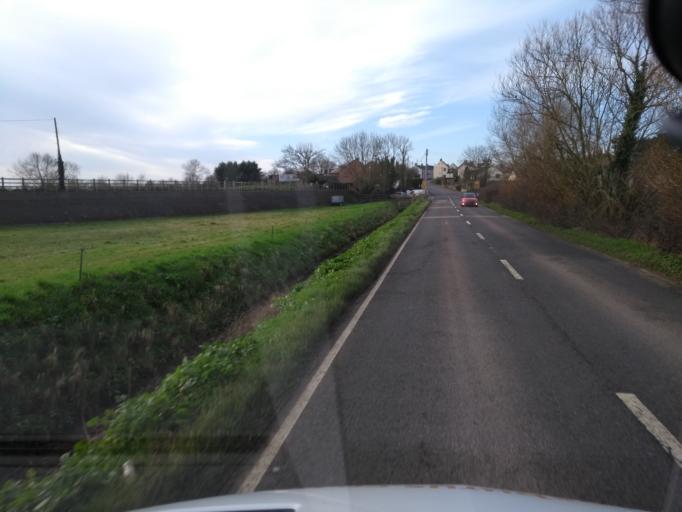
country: GB
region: England
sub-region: Somerset
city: Westonzoyland
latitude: 51.0576
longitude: -2.9479
